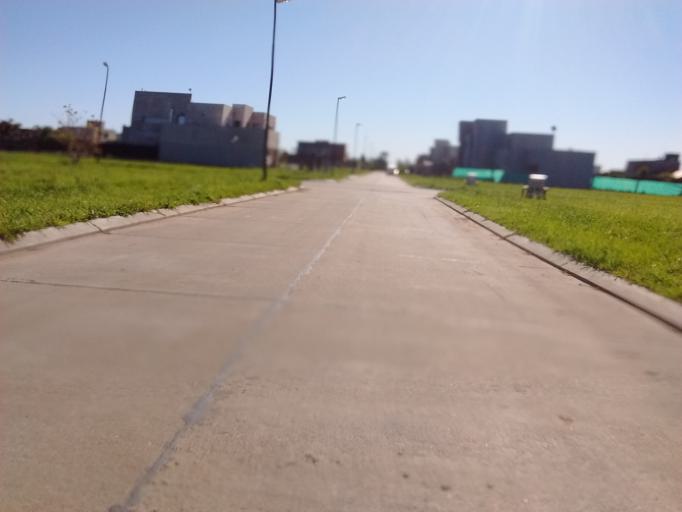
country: AR
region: Santa Fe
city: Funes
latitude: -32.9258
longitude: -60.8454
